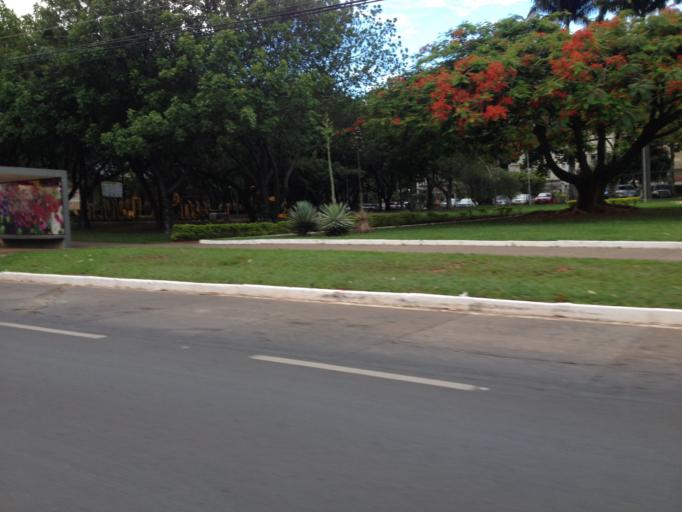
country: BR
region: Federal District
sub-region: Brasilia
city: Brasilia
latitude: -15.8088
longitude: -47.9455
